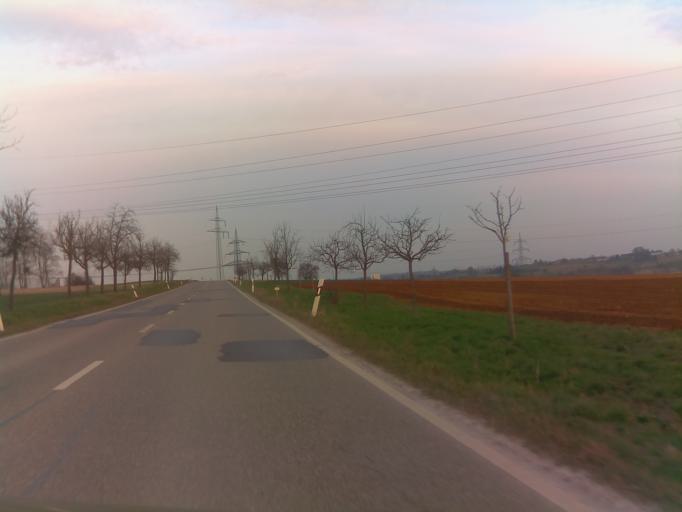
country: DE
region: Baden-Wuerttemberg
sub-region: Regierungsbezirk Stuttgart
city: Oberriexingen
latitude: 48.9015
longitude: 9.0471
